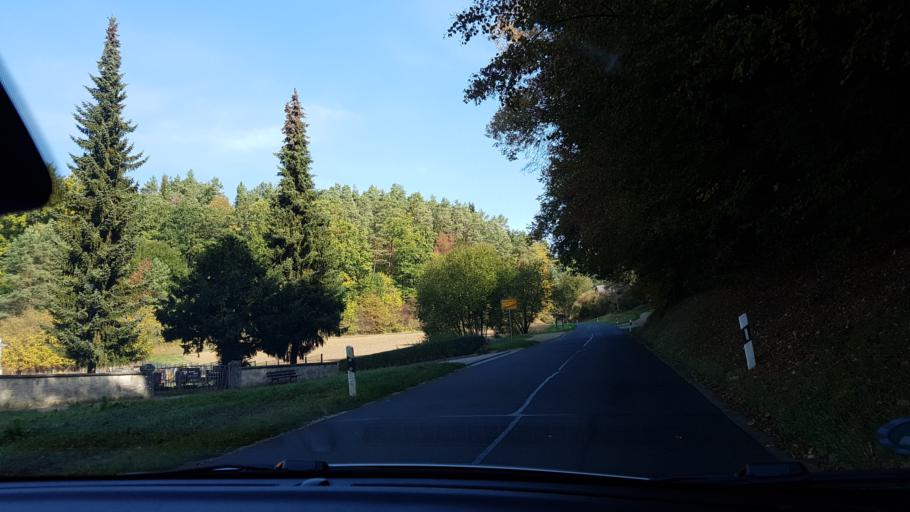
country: DE
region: Bavaria
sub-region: Upper Franconia
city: Waischenfeld
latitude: 49.8154
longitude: 11.3540
